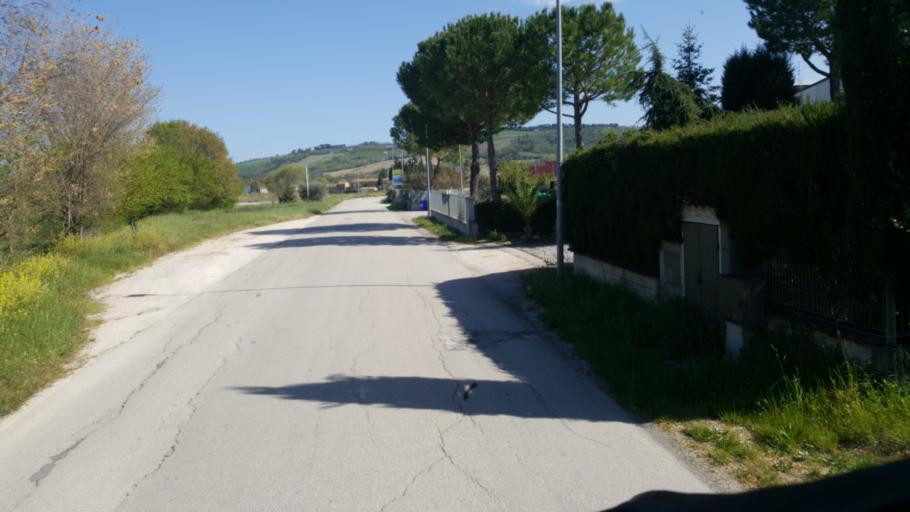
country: IT
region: The Marches
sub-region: Provincia di Macerata
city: Montecassiano
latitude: 43.3545
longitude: 13.4647
